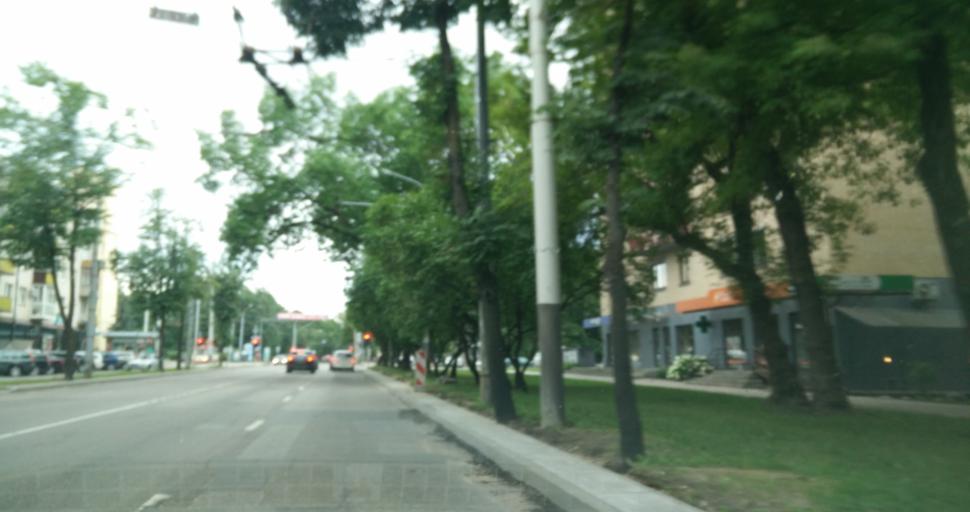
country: LT
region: Vilnius County
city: Rasos
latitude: 54.7127
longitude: 25.3151
